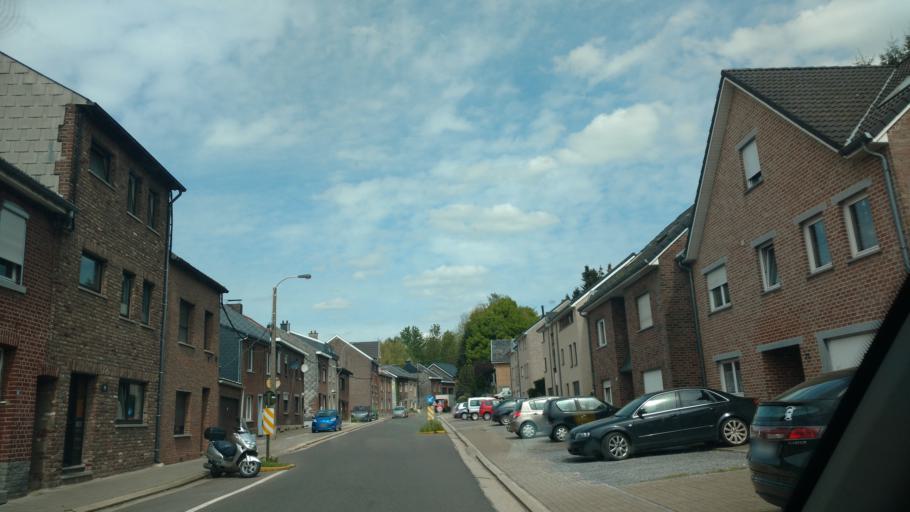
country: BE
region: Wallonia
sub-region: Province de Liege
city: Plombieres
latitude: 50.7401
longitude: 5.9895
